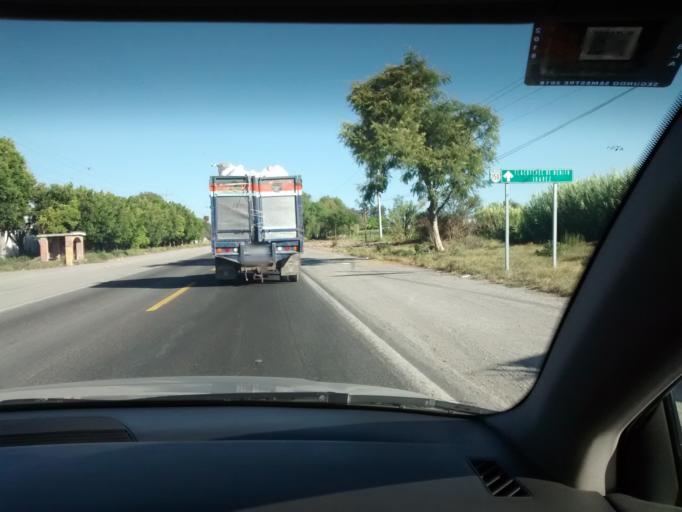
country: MX
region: Puebla
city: San Bartolo Teontepec
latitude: 18.5321
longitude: -97.5239
